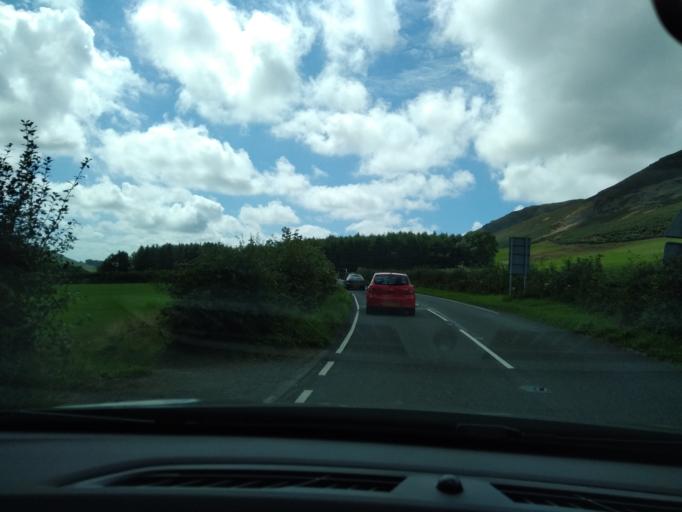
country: GB
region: England
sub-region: Cumbria
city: Millom
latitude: 54.2485
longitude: -3.3066
